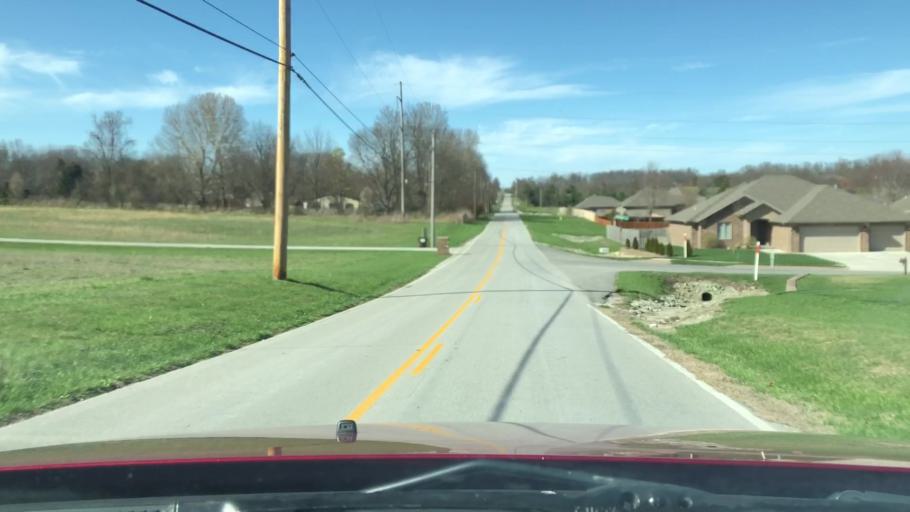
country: US
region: Missouri
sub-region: Greene County
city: Strafford
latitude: 37.2291
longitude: -93.1884
